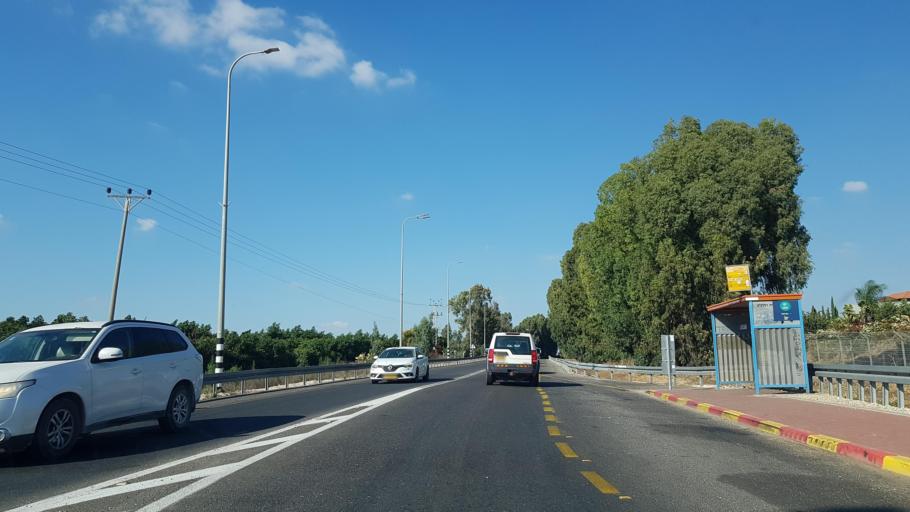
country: PS
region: West Bank
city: Tulkarm
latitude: 32.3258
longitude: 35.0013
